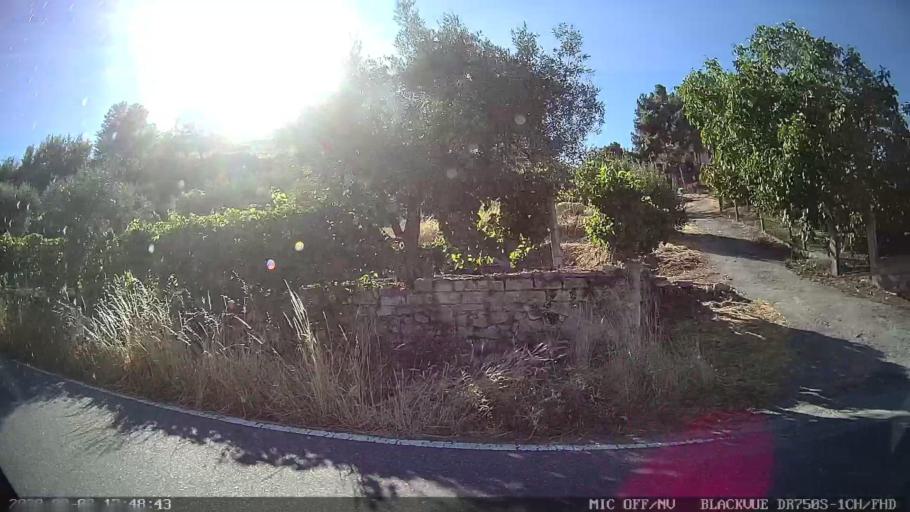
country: PT
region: Vila Real
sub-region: Murca
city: Murca
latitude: 41.4035
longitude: -7.4772
